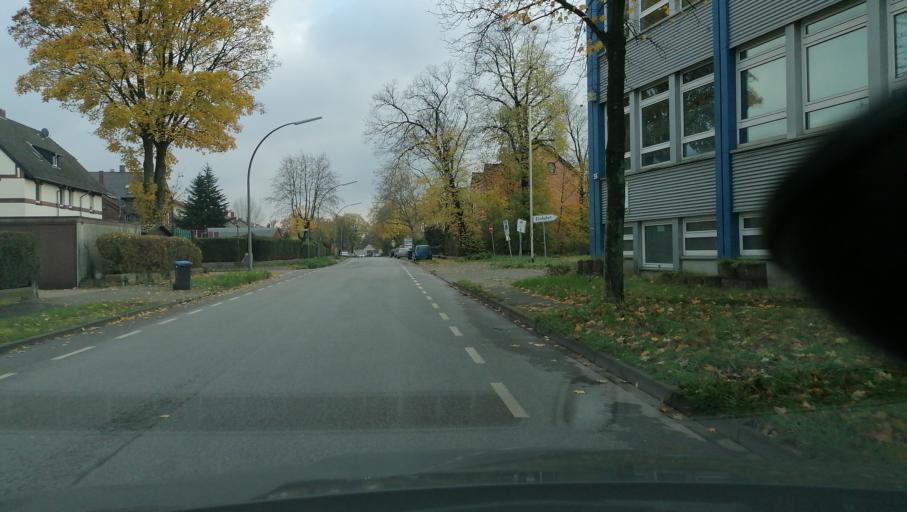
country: DE
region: North Rhine-Westphalia
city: Herten
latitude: 51.5645
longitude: 7.1811
